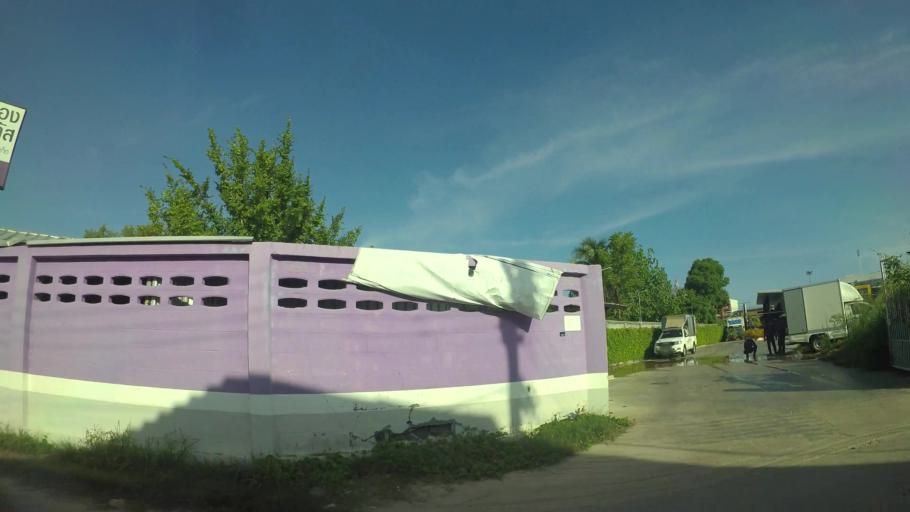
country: TH
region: Bangkok
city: Lat Krabang
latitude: 13.7128
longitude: 100.7664
